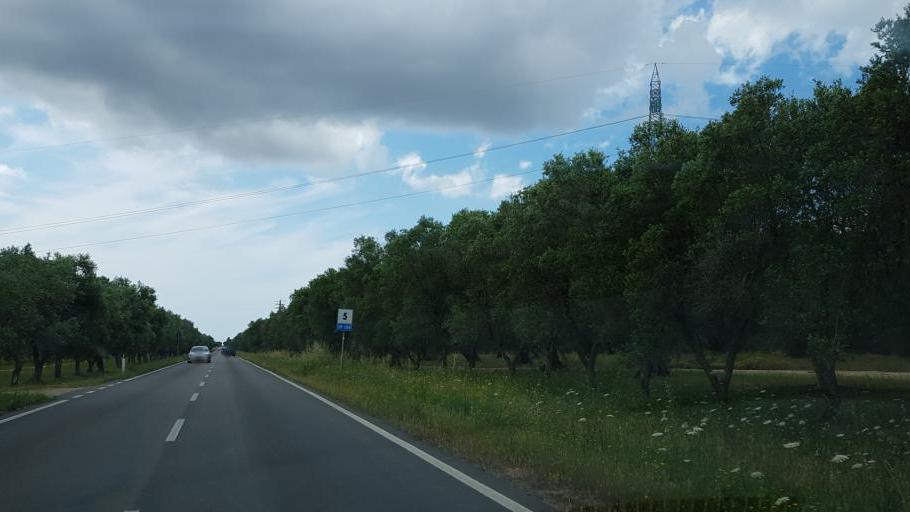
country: IT
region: Apulia
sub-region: Provincia di Brindisi
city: San Pancrazio Salentino
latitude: 40.3617
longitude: 17.8423
